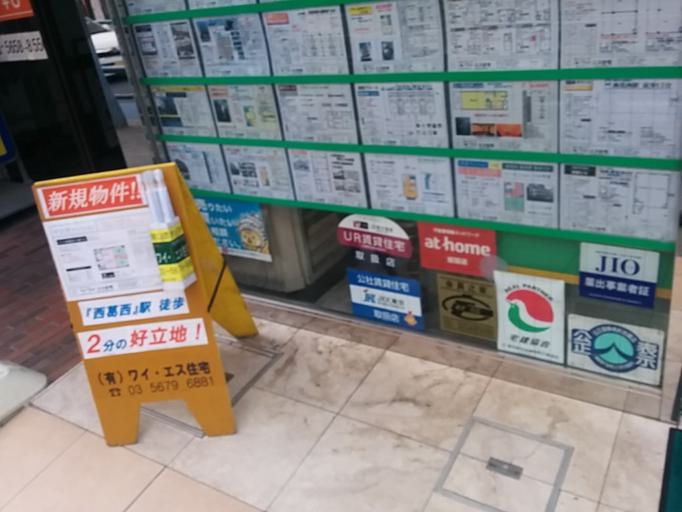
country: JP
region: Tokyo
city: Urayasu
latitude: 35.6636
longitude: 139.8588
